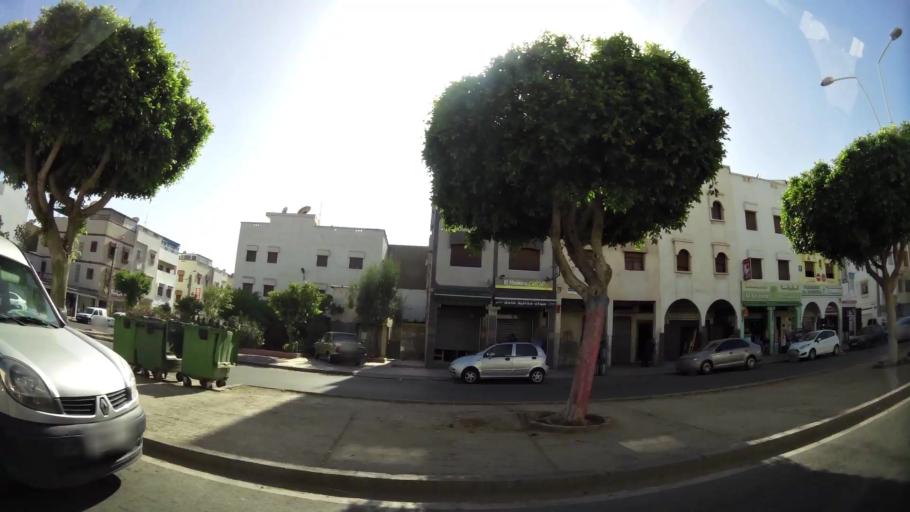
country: MA
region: Oued ed Dahab-Lagouira
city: Dakhla
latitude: 30.4108
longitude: -9.5677
